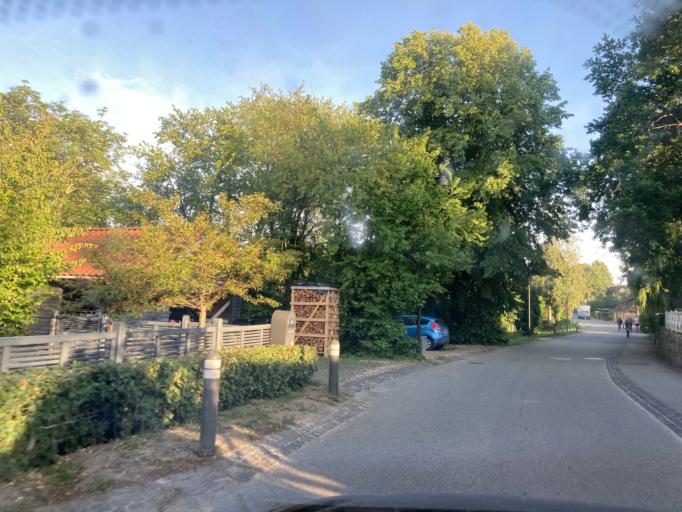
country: DK
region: Zealand
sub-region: Lejre Kommune
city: Lejre
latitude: 55.6455
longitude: 11.9607
